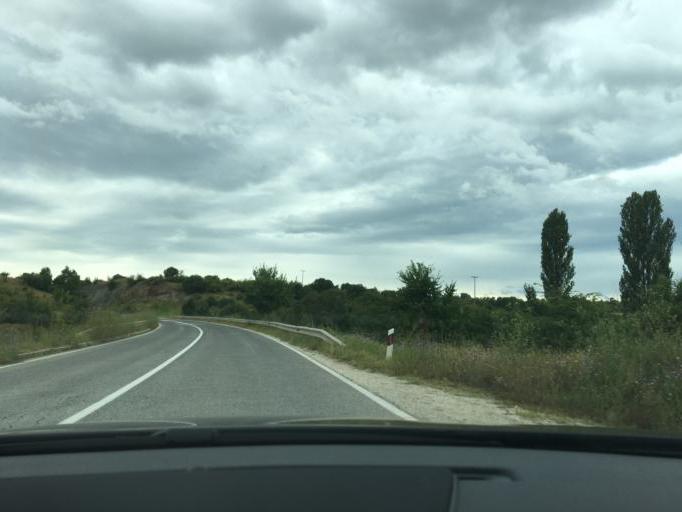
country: MK
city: Klechovce
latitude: 42.1561
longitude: 21.9498
